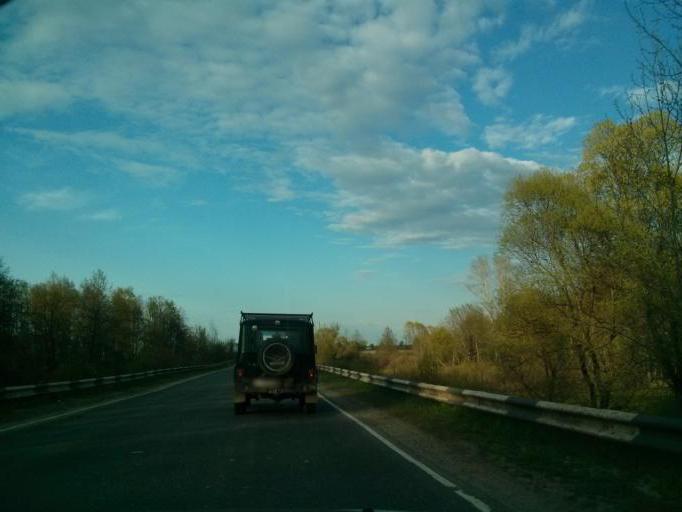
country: RU
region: Nizjnij Novgorod
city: Navashino
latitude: 55.6178
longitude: 42.2267
